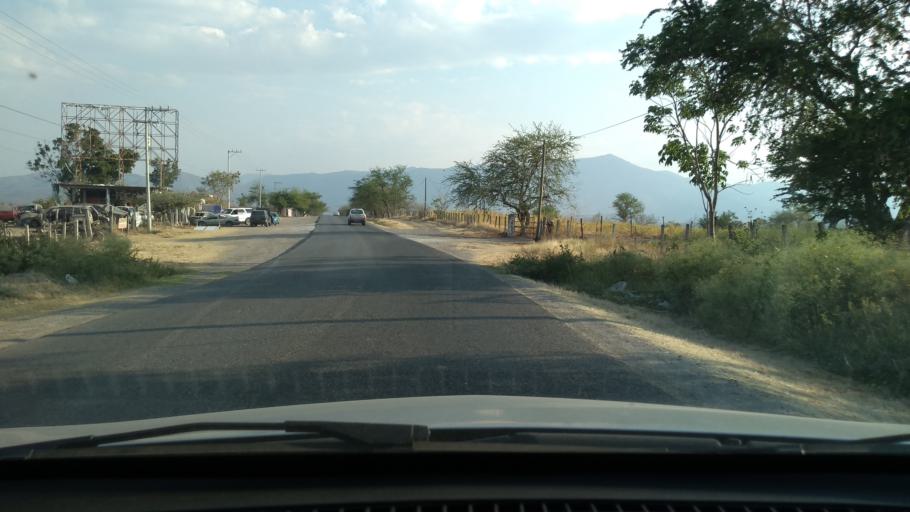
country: MX
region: Morelos
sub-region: Jojutla
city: Tehuixtla
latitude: 18.5846
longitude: -99.2642
